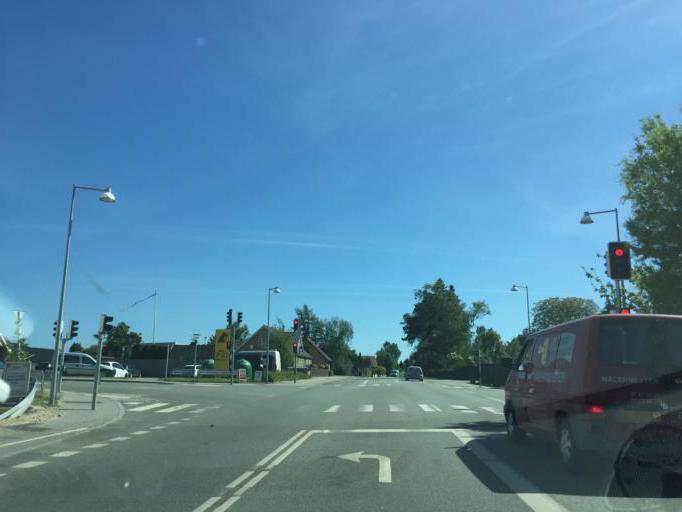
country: DK
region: Zealand
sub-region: Stevns Kommune
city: Stroby Egede
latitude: 55.4165
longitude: 12.2433
